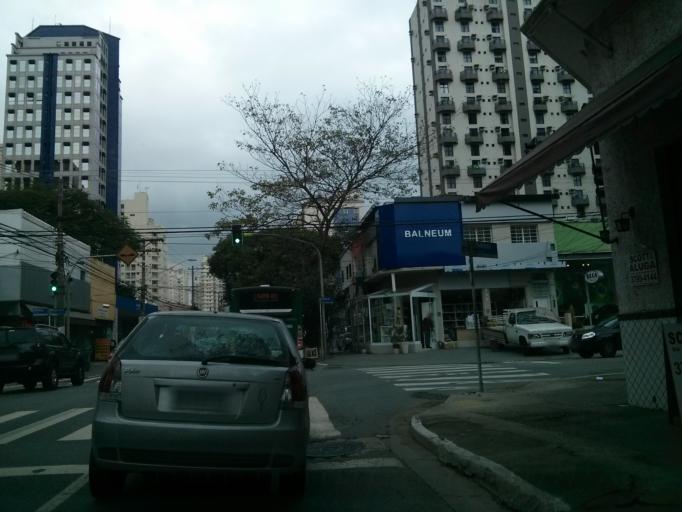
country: BR
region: Sao Paulo
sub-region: Sao Paulo
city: Sao Paulo
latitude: -23.6036
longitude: -46.6577
